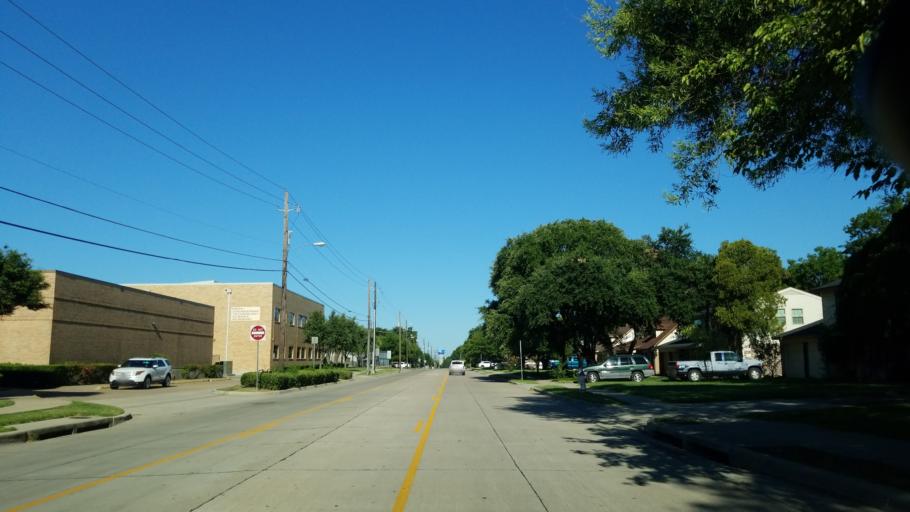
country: US
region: Texas
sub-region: Dallas County
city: Carrollton
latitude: 32.9491
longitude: -96.8916
